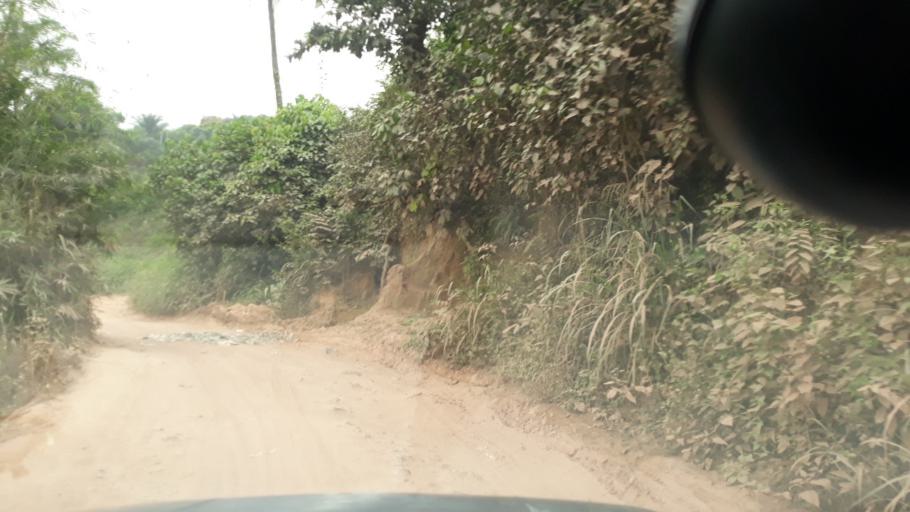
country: CD
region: Bas-Congo
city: Kasangulu
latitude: -4.4783
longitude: 15.2730
